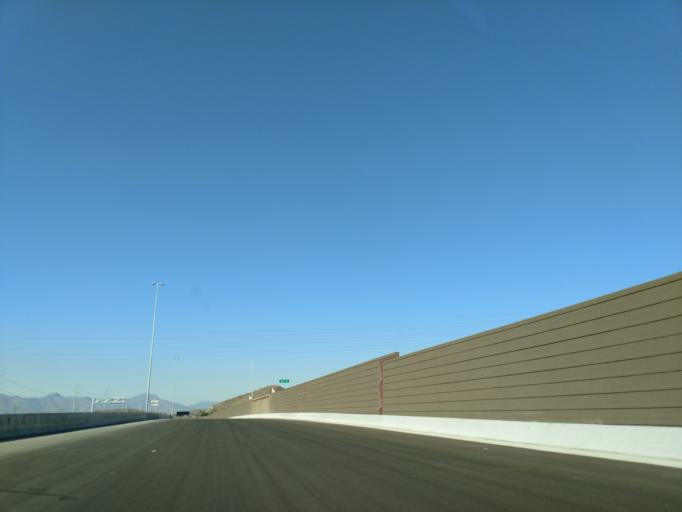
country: US
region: Arizona
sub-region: Maricopa County
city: Guadalupe
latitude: 33.2922
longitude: -112.0305
